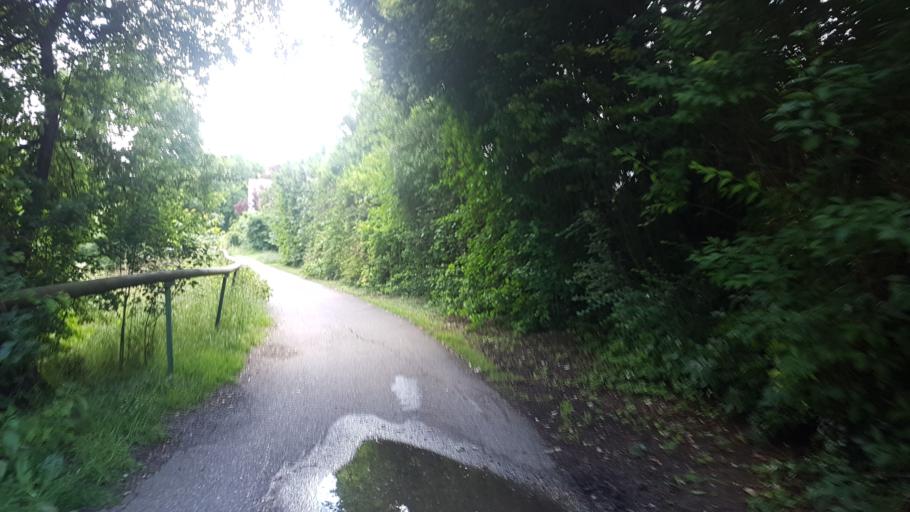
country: DE
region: Bavaria
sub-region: Upper Bavaria
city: Eichstaett
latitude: 48.8928
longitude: 11.1642
